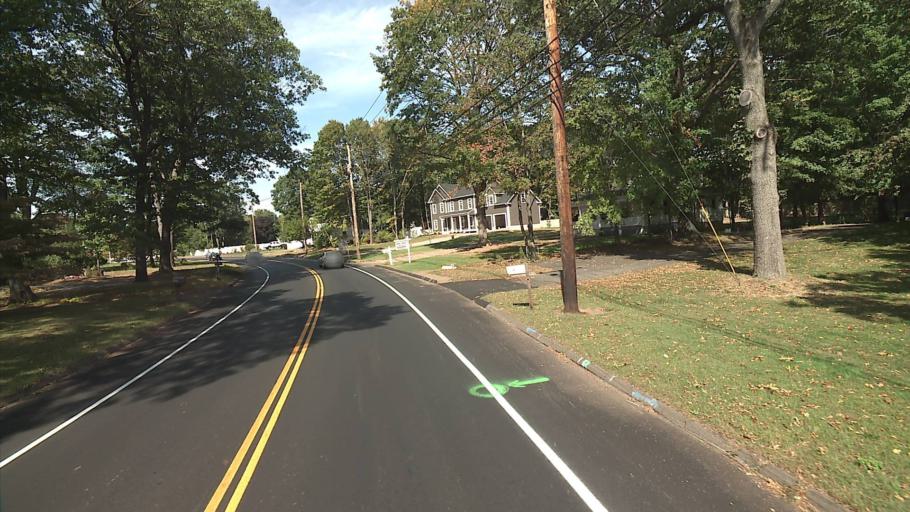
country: US
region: Connecticut
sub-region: New Haven County
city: North Haven
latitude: 41.3747
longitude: -72.8520
